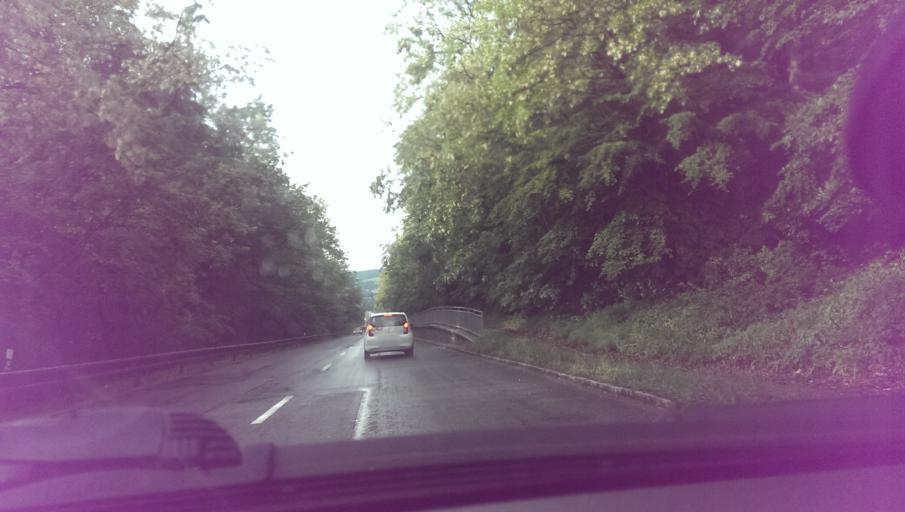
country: CZ
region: Zlin
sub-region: Okres Zlin
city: Zlin
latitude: 49.2141
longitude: 17.6612
